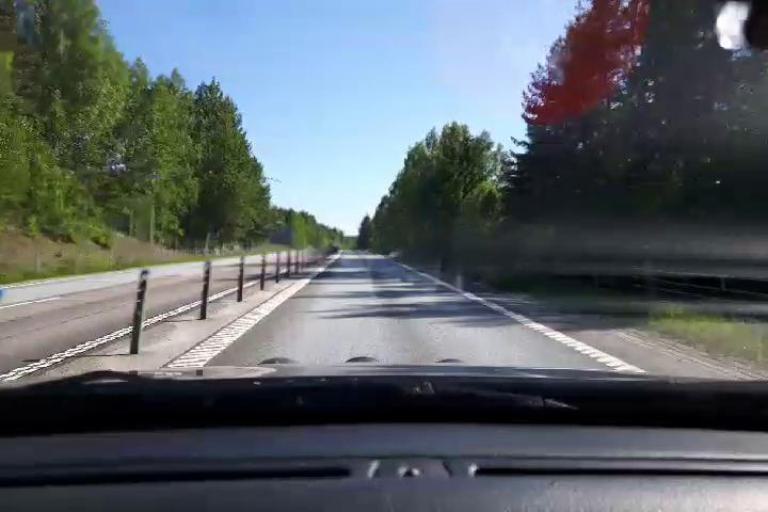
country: SE
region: Gaevleborg
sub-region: Soderhamns Kommun
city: Soderhamn
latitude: 61.2878
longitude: 17.0235
